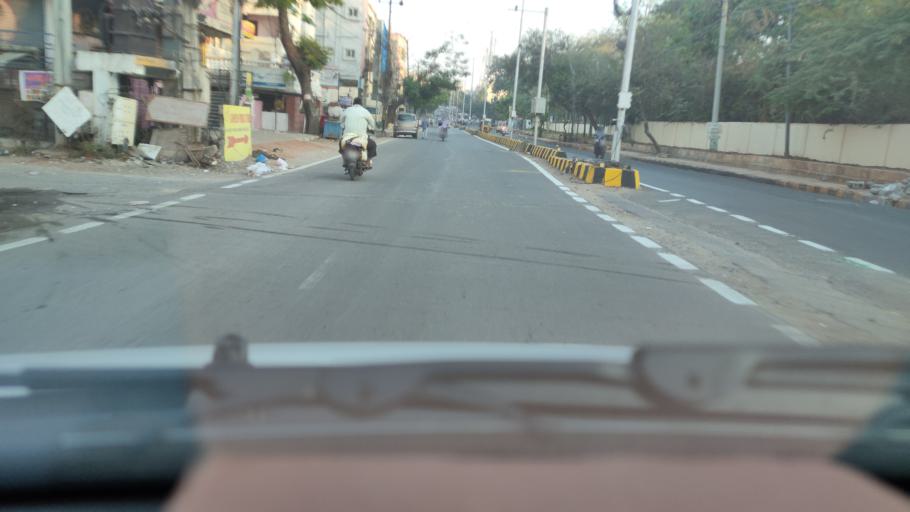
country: IN
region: Telangana
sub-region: Rangareddi
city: Gaddi Annaram
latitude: 17.3884
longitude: 78.5164
